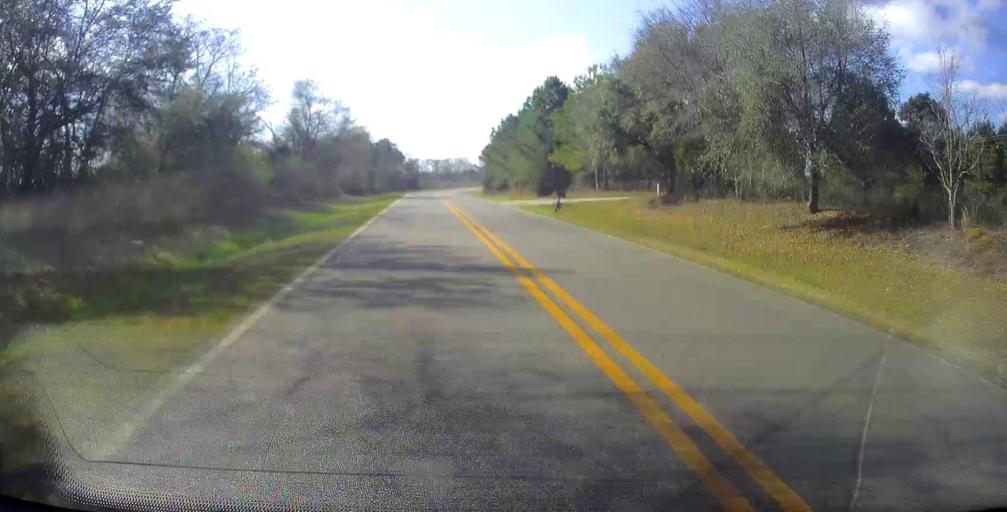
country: US
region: Georgia
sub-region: Laurens County
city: Dublin
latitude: 32.5695
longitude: -83.0374
